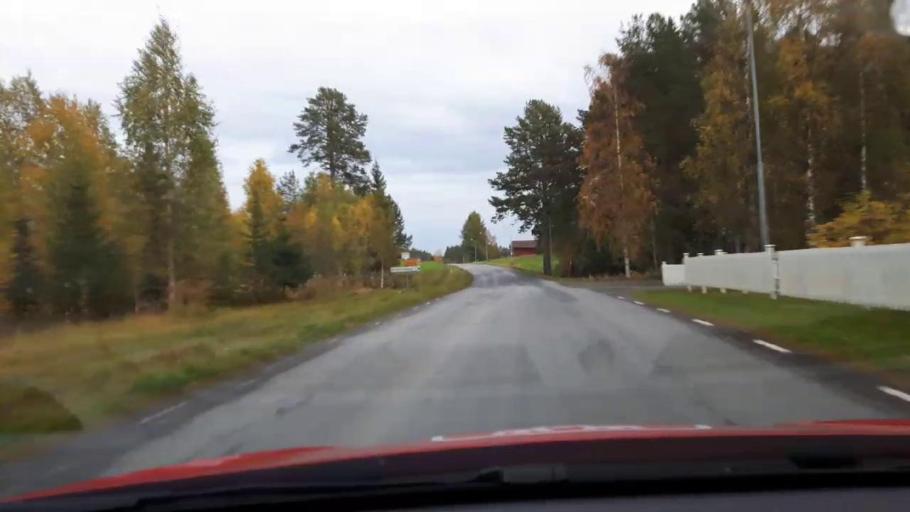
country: SE
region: Jaemtland
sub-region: OEstersunds Kommun
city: Lit
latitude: 63.3141
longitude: 14.9866
